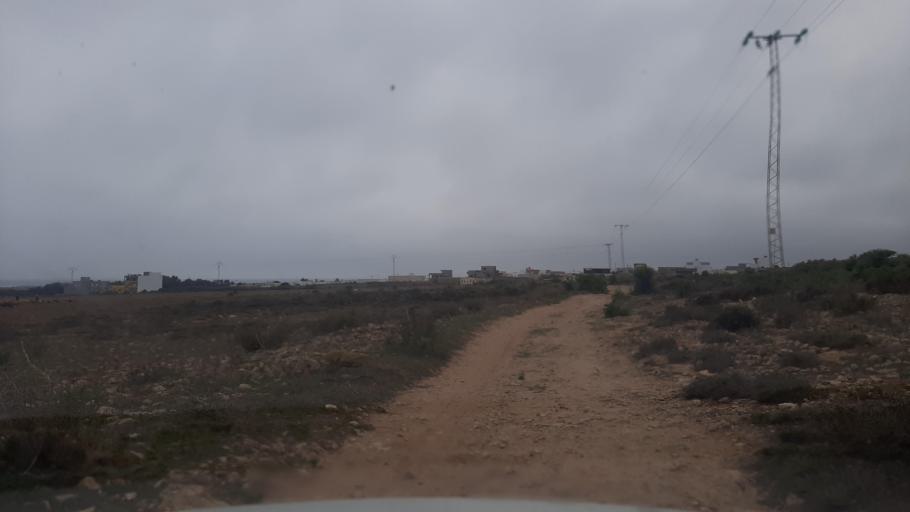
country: TN
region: Nabul
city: Menzel Heurr
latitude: 36.6874
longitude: 10.9314
